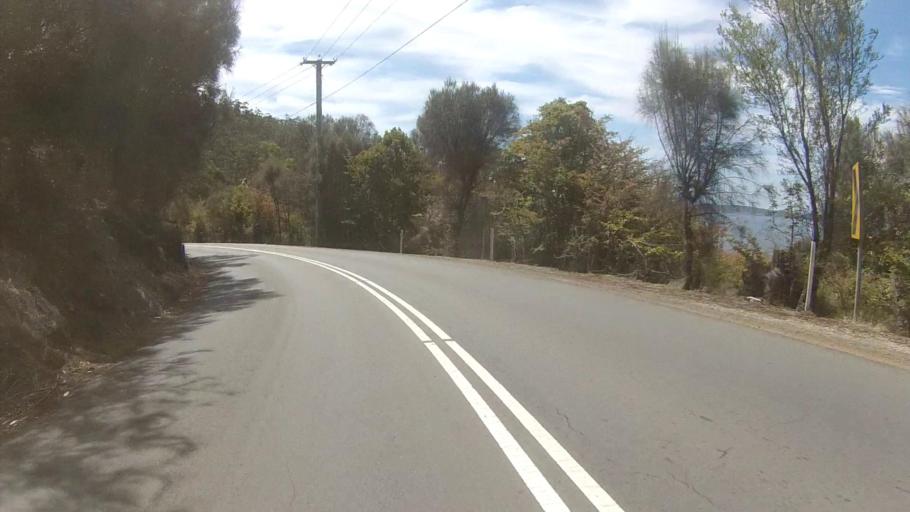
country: AU
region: Tasmania
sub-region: Kingborough
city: Kingston Beach
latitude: -42.9610
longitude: 147.3313
